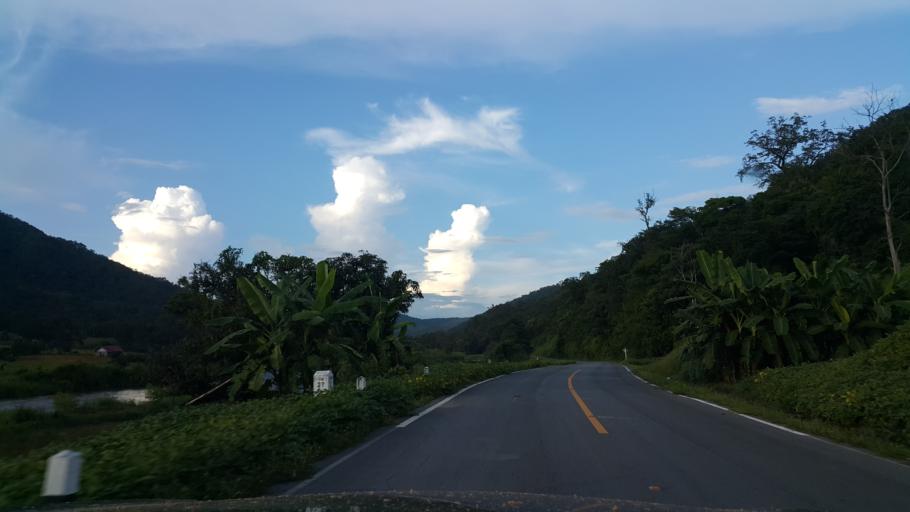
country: TH
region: Mae Hong Son
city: Mae Hi
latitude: 19.2247
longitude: 98.4394
